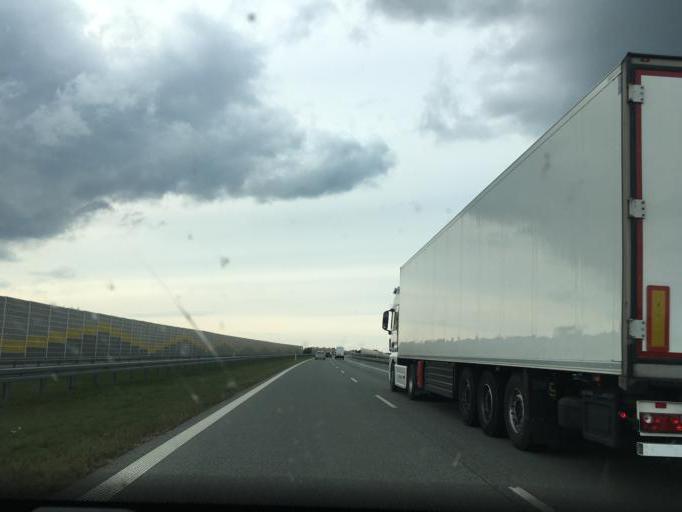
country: PL
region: Lodz Voivodeship
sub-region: Powiat zdunskowolski
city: Zdunska Wola
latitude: 51.5774
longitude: 18.9212
